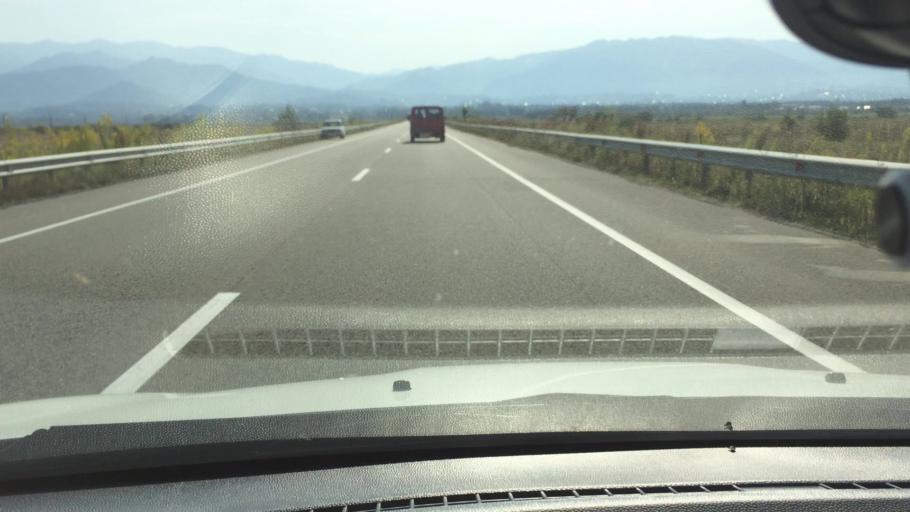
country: GE
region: Ajaria
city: Ochkhamuri
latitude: 41.8753
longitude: 41.8257
